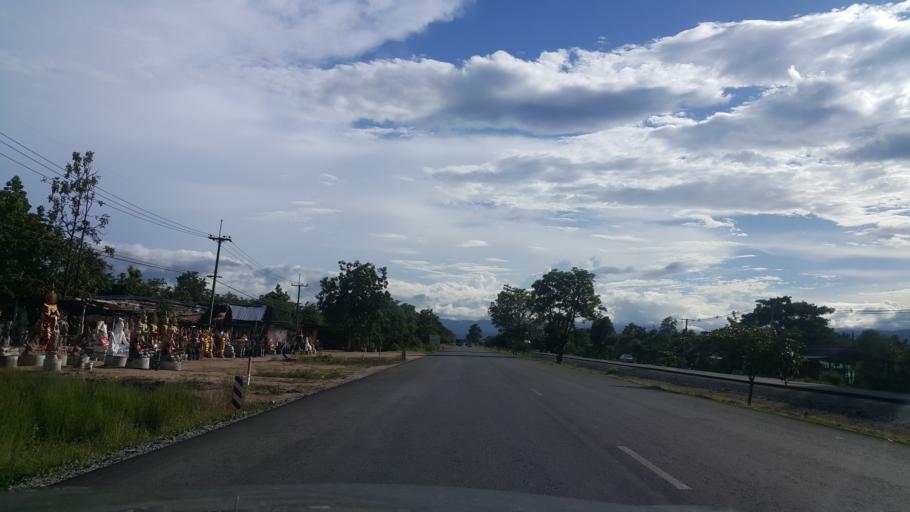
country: TH
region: Tak
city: Ban Tak
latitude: 17.1403
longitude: 99.1163
